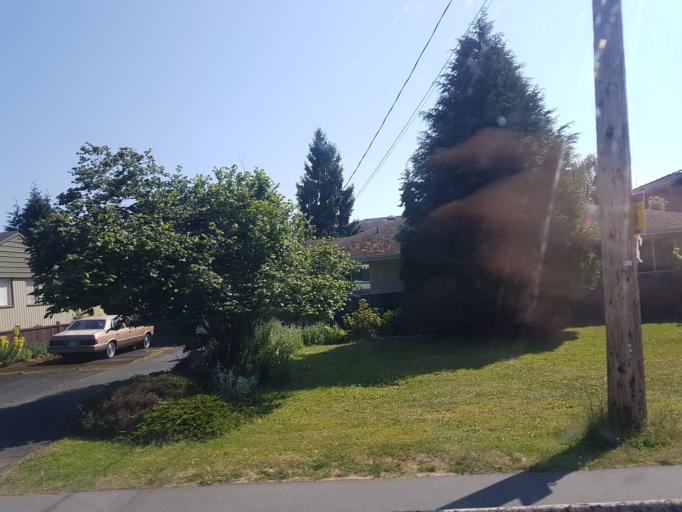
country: CA
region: British Columbia
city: Oak Bay
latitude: 48.4911
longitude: -123.3239
